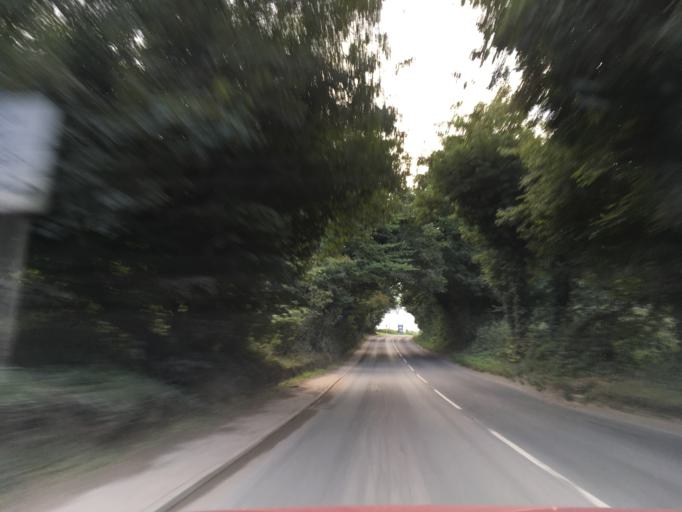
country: GB
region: England
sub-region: Wiltshire
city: Devizes
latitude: 51.3397
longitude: -1.9696
